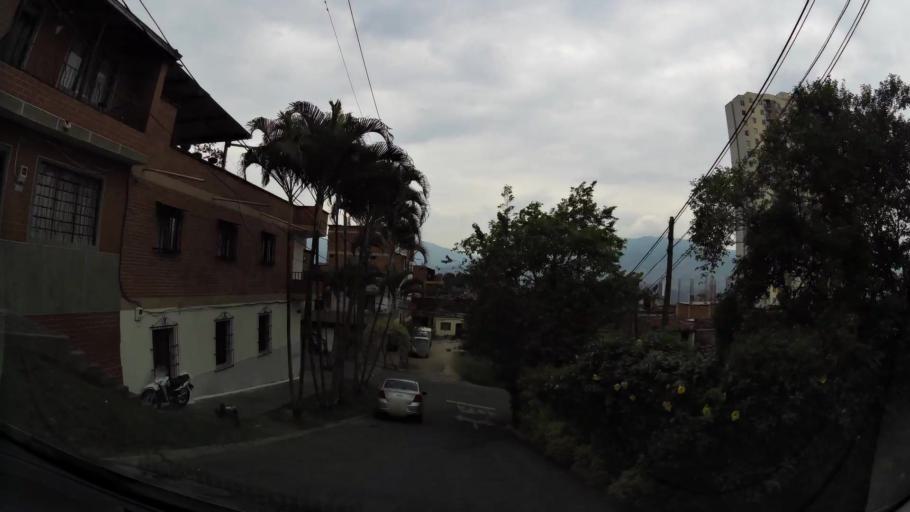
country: CO
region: Antioquia
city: Medellin
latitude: 6.2378
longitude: -75.5569
